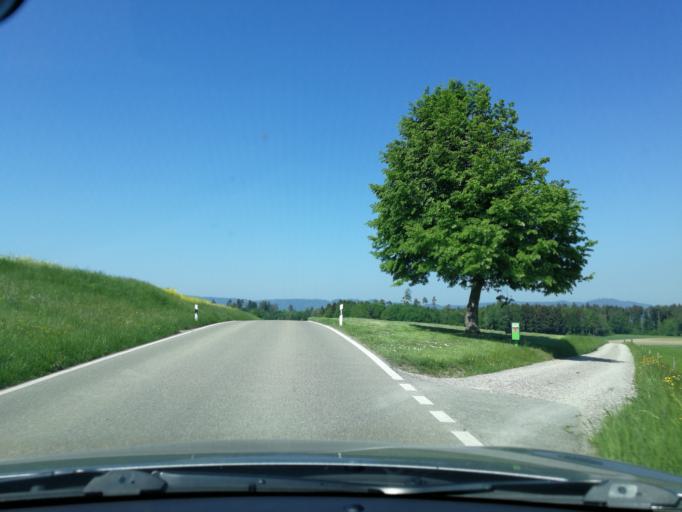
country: CH
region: Zurich
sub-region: Bezirk Meilen
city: Zumikon
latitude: 47.3172
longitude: 8.6246
